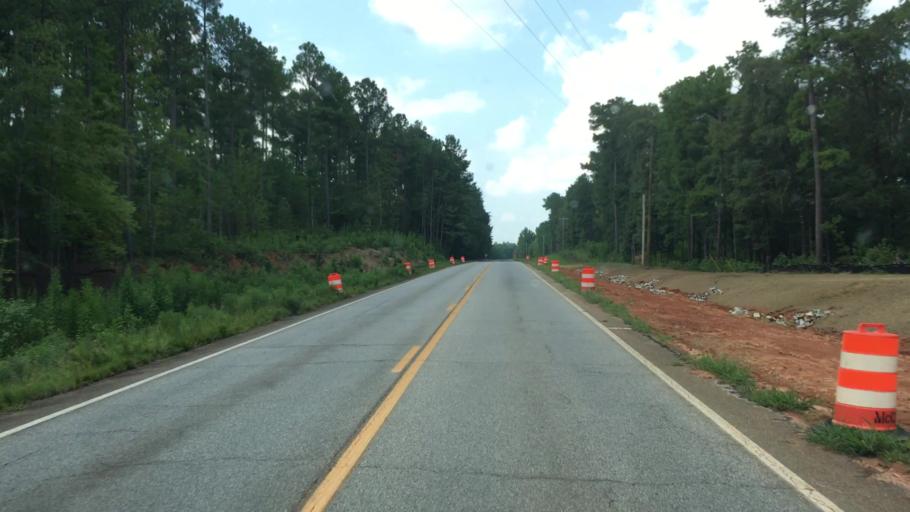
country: US
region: Georgia
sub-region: Monroe County
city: Forsyth
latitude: 33.1181
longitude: -83.8709
